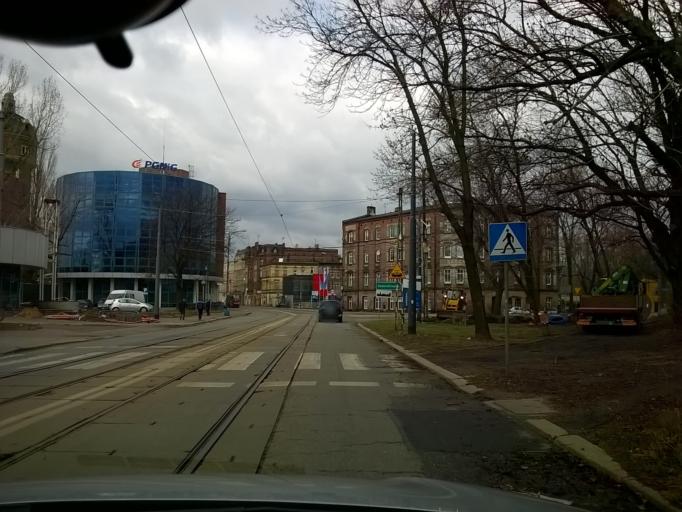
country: PL
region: Silesian Voivodeship
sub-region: Swietochlowice
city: Swietochlowice
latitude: 50.2839
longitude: 18.9352
